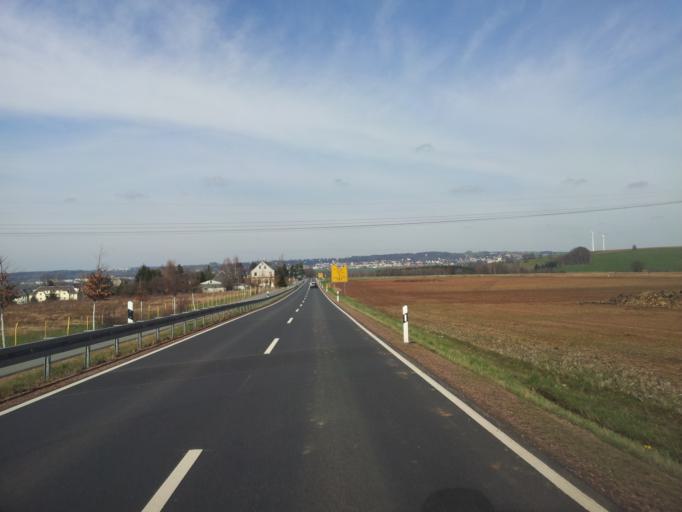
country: DE
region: Saxony
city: Gersdorf
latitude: 50.7566
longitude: 12.7193
